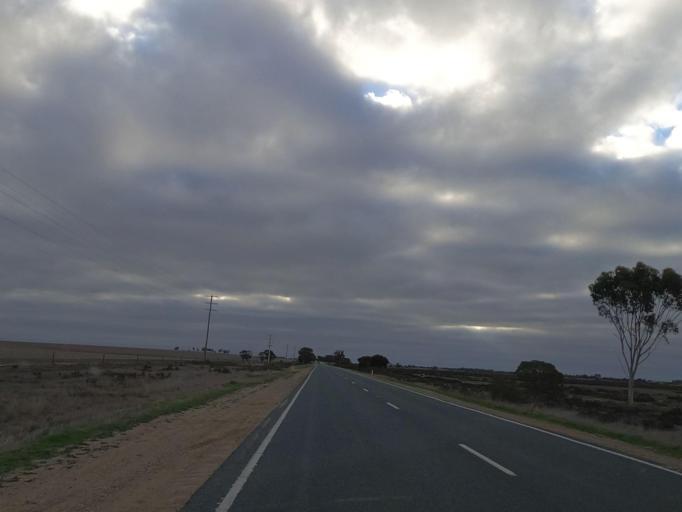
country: AU
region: Victoria
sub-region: Swan Hill
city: Swan Hill
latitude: -35.6382
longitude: 143.8260
